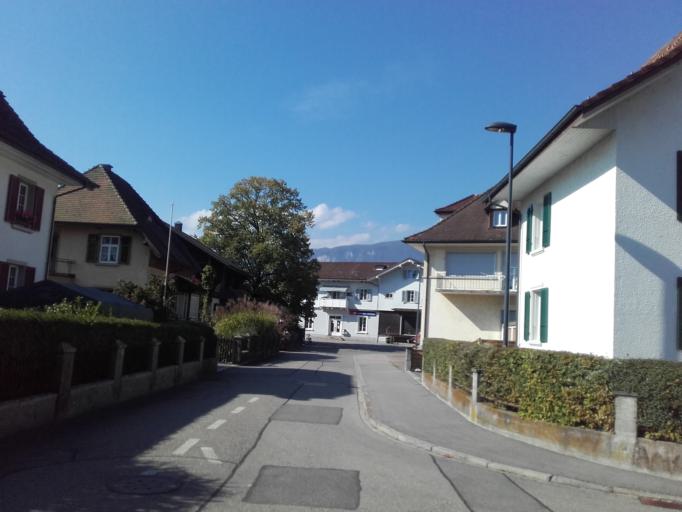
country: CH
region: Solothurn
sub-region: Bezirk Wasseramt
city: Luterbach
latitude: 47.2166
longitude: 7.5845
